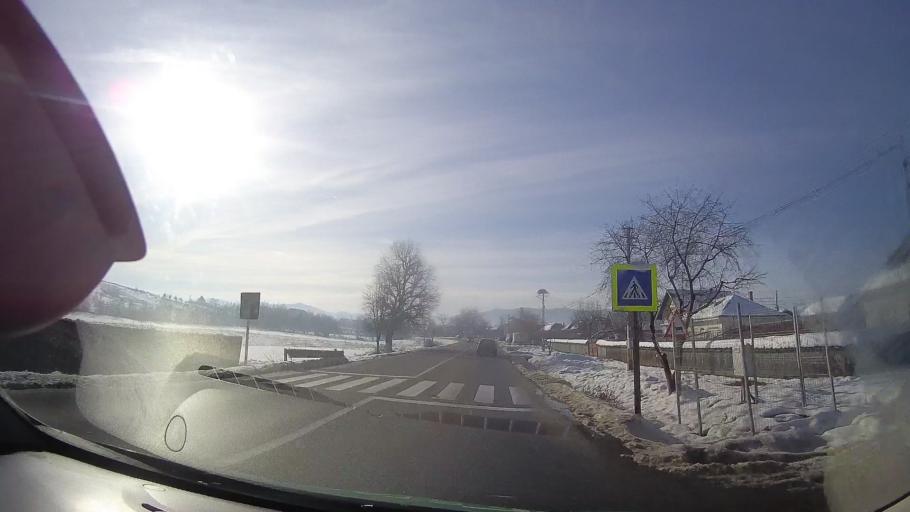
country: RO
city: Vanatori-Neamt
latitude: 47.1843
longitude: 26.3337
